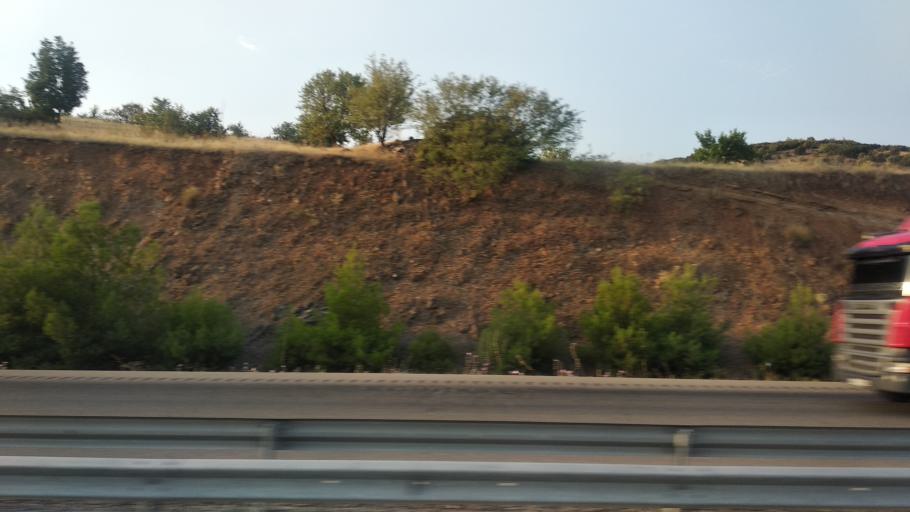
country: TR
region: Manisa
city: Menye
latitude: 38.5672
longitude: 28.5662
